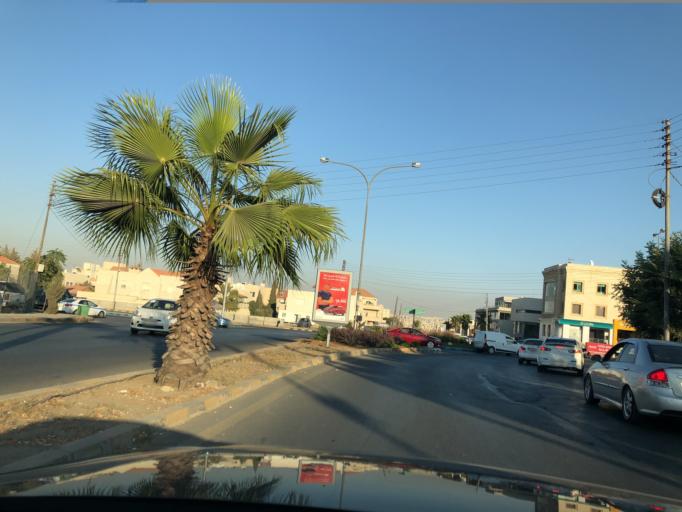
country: JO
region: Amman
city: Al Bunayyat ash Shamaliyah
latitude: 31.9426
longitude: 35.8798
